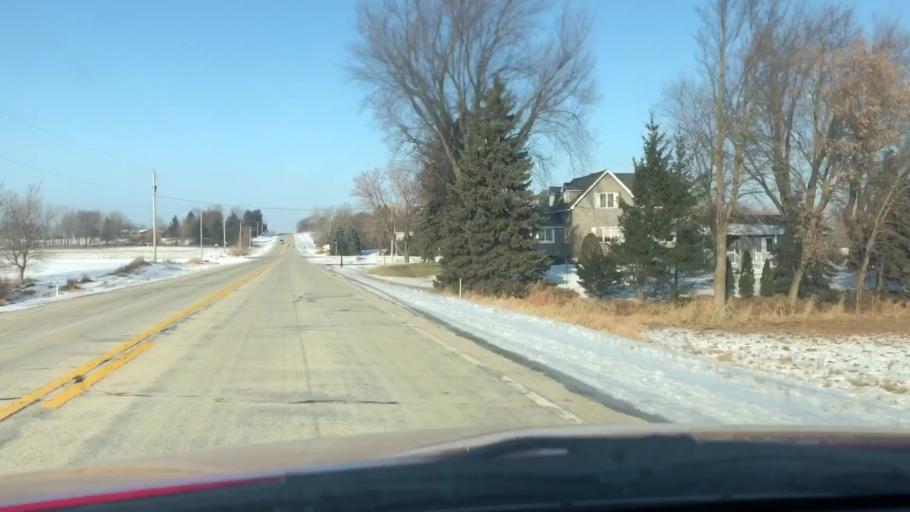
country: US
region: Wisconsin
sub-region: Outagamie County
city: Kimberly
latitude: 44.3715
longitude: -88.3745
